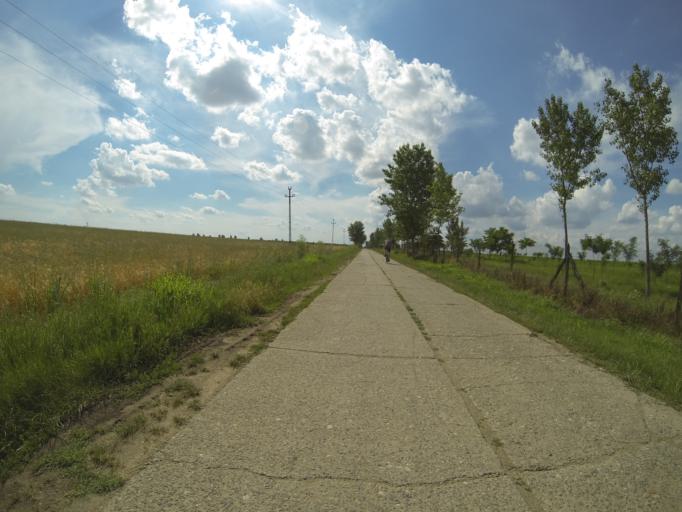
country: RO
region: Dolj
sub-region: Comuna Segarcea
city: Segarcea
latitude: 44.1083
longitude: 23.7338
